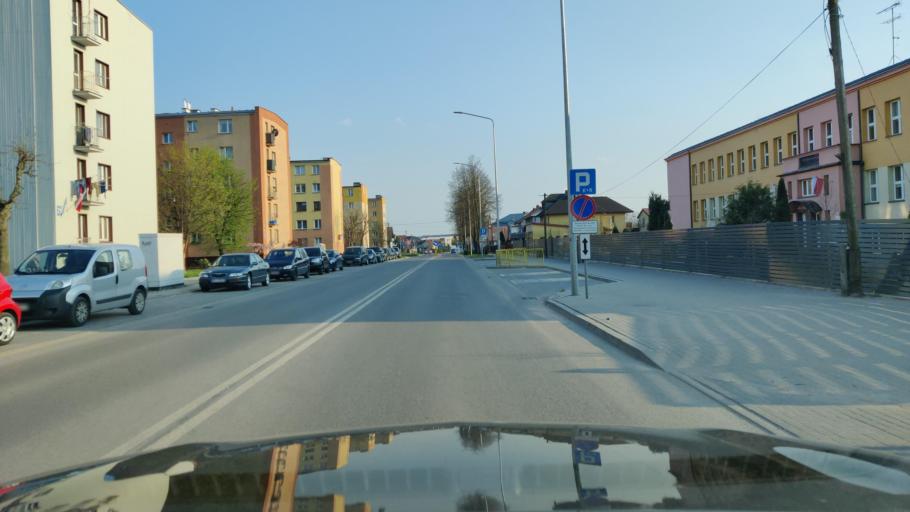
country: PL
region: Masovian Voivodeship
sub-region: Powiat pultuski
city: Pultusk
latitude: 52.7047
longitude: 21.0763
